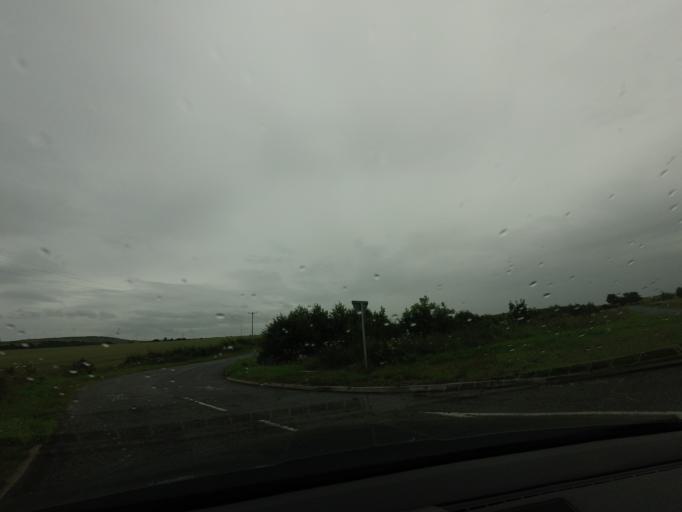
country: GB
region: Scotland
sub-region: Aberdeenshire
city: Portsoy
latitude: 57.6410
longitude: -2.6506
